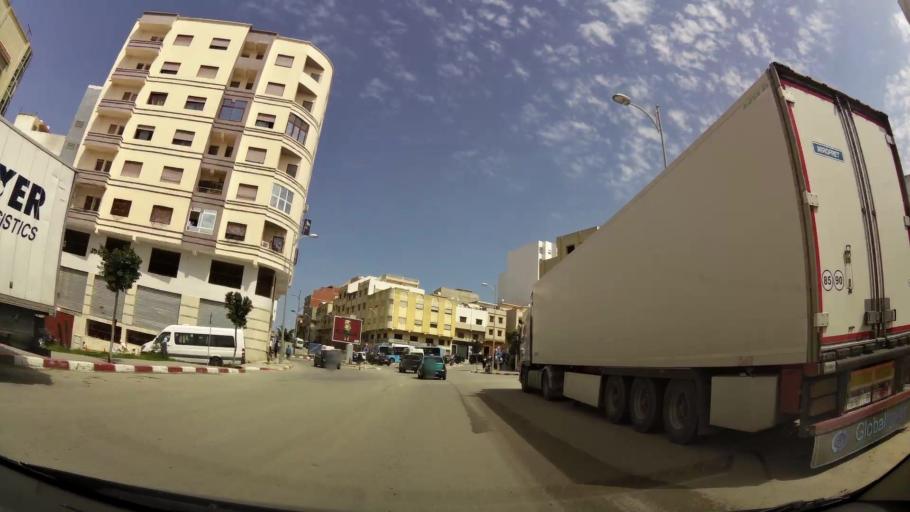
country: MA
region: Tanger-Tetouan
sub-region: Tanger-Assilah
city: Tangier
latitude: 35.7428
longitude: -5.8305
